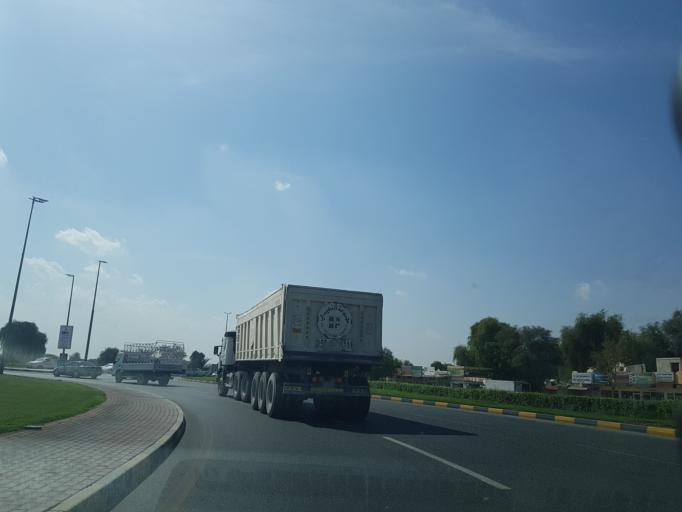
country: AE
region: Ra's al Khaymah
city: Ras al-Khaimah
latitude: 25.7138
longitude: 55.9704
